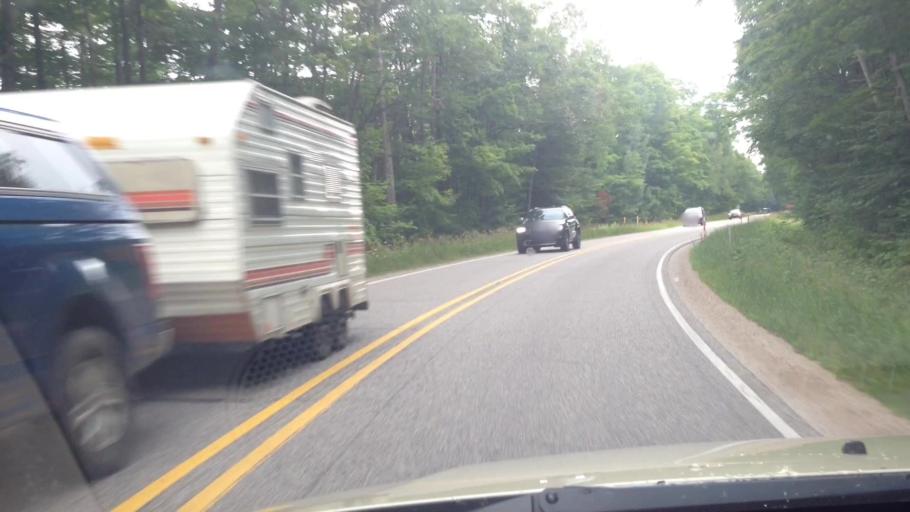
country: US
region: Michigan
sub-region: Mackinac County
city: Saint Ignace
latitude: 46.0459
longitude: -85.1122
